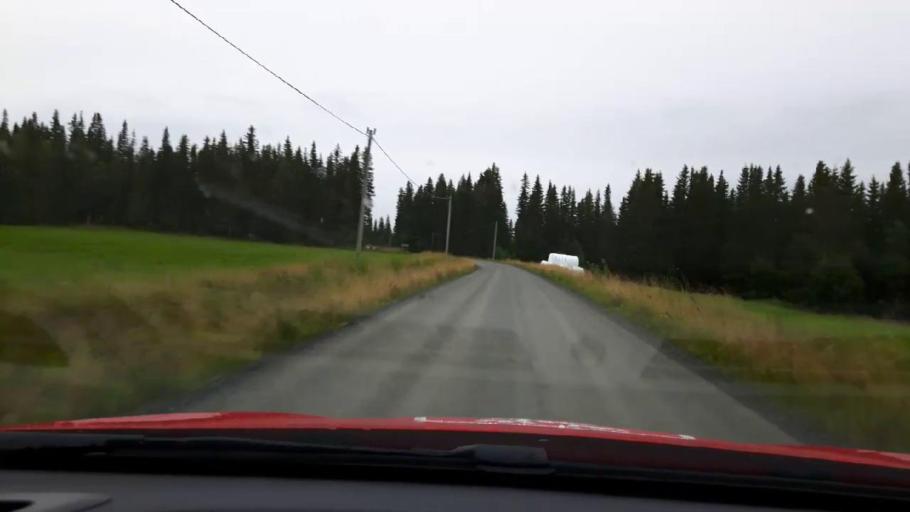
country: SE
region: Jaemtland
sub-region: Are Kommun
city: Are
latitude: 63.4283
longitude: 12.8048
